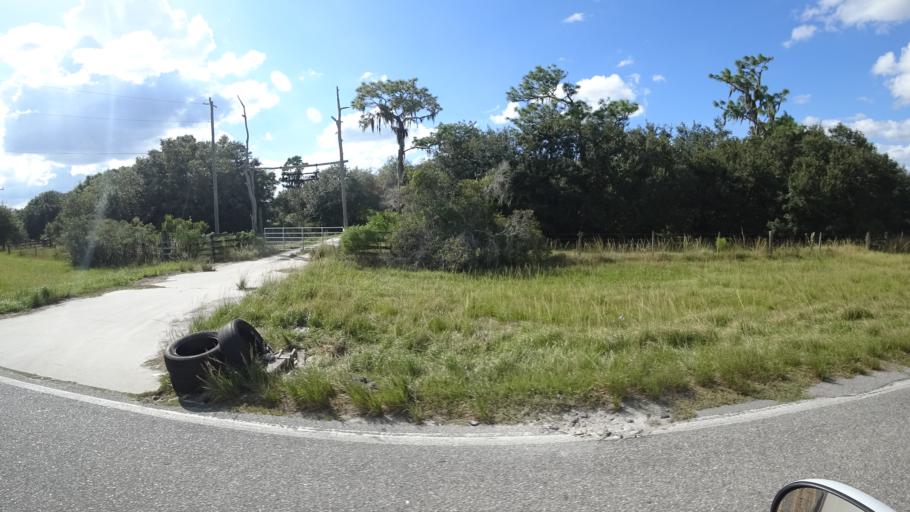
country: US
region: Florida
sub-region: DeSoto County
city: Nocatee
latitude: 27.2812
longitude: -82.1135
